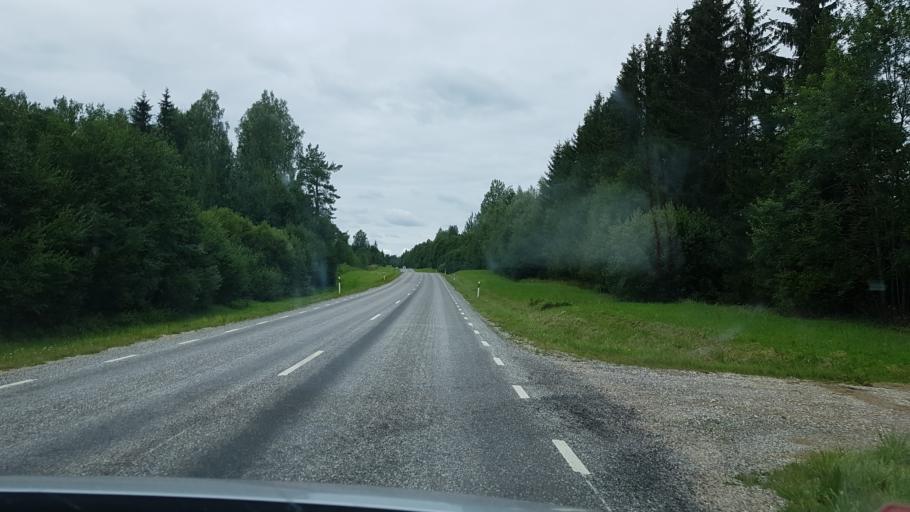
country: EE
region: Vorumaa
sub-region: Antsla vald
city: Vana-Antsla
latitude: 58.0026
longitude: 26.7065
